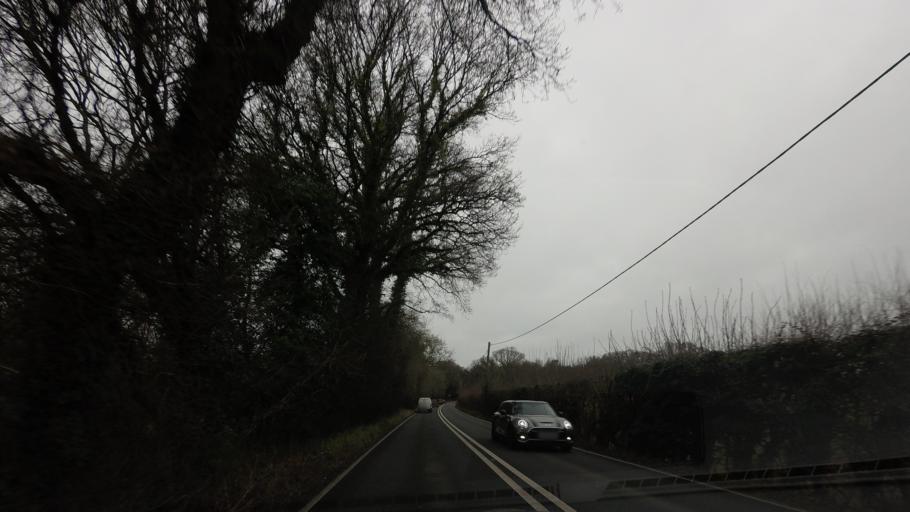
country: GB
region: England
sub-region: East Sussex
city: Battle
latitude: 50.9160
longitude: 0.5390
